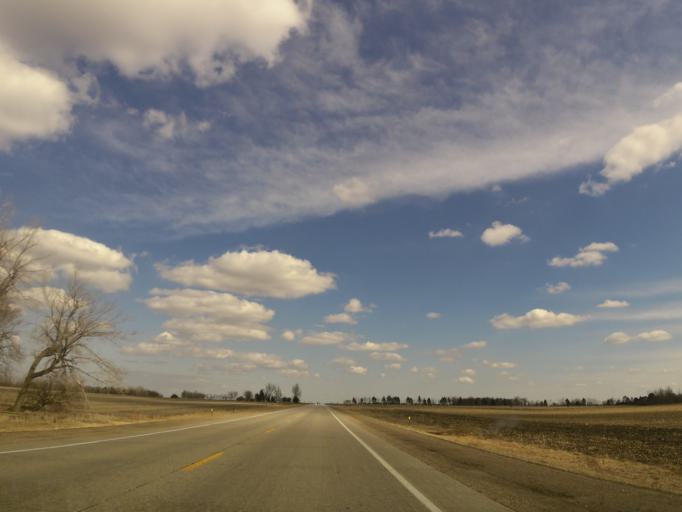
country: US
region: South Dakota
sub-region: Deuel County
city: Clear Lake
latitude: 44.8900
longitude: -96.8590
